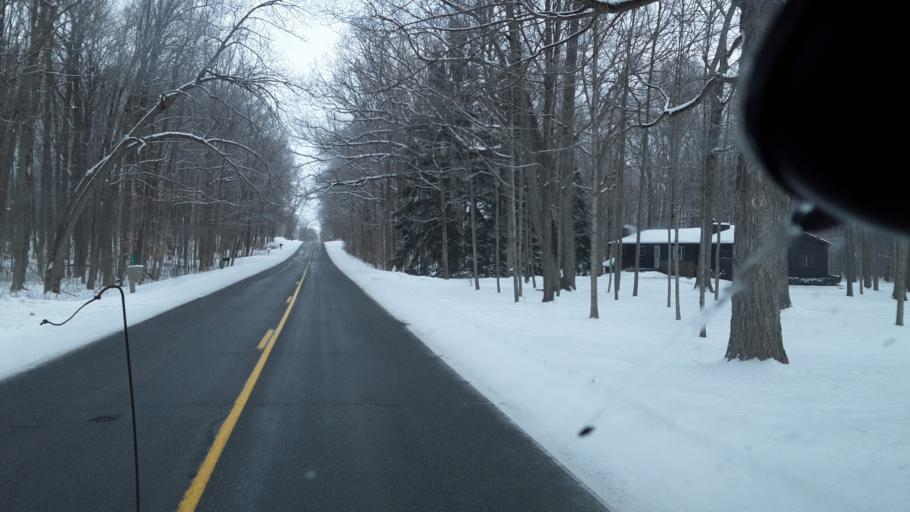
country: US
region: Michigan
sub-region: Eaton County
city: Dimondale
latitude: 42.6328
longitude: -84.6029
